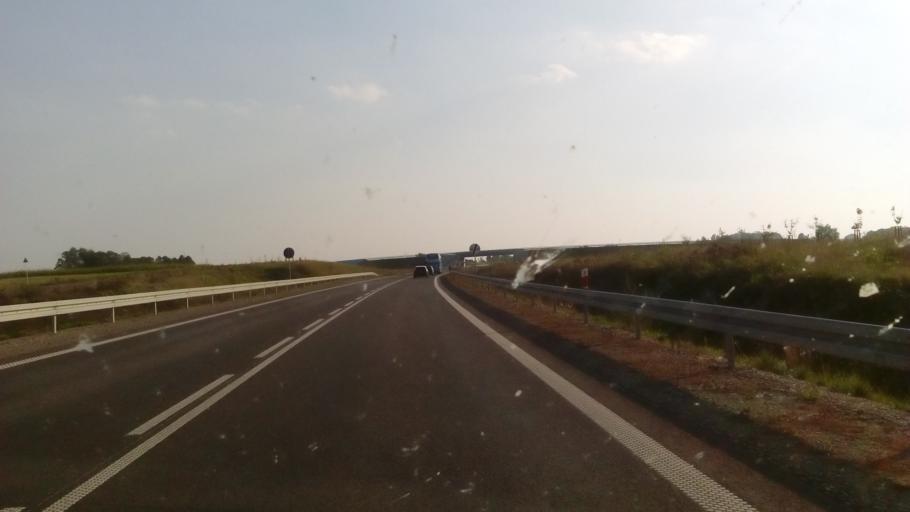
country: PL
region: Podlasie
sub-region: Powiat grajewski
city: Rajgrod
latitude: 53.7685
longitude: 22.8326
